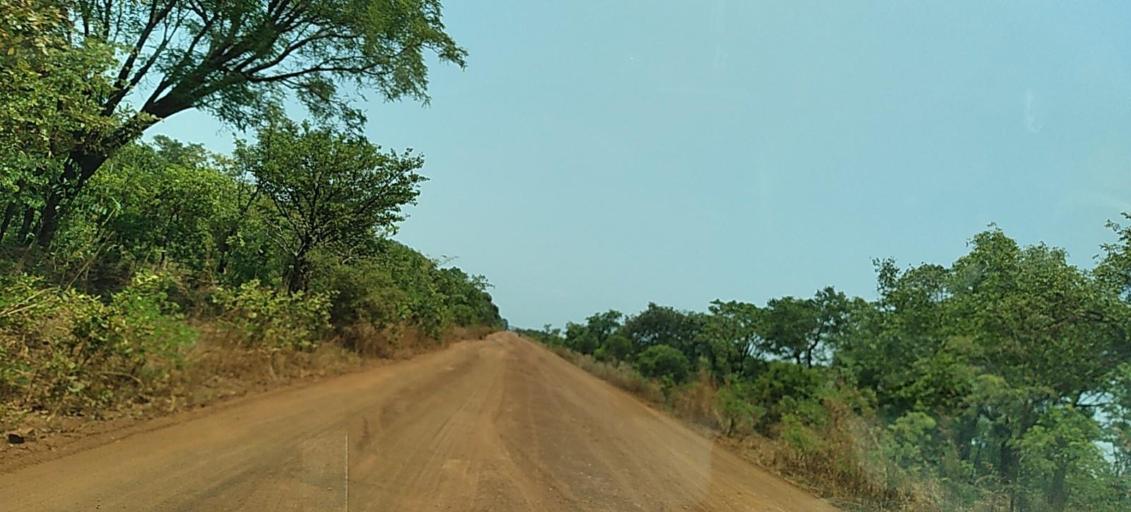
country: ZM
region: Copperbelt
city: Mpongwe
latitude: -13.6866
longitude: 27.8603
